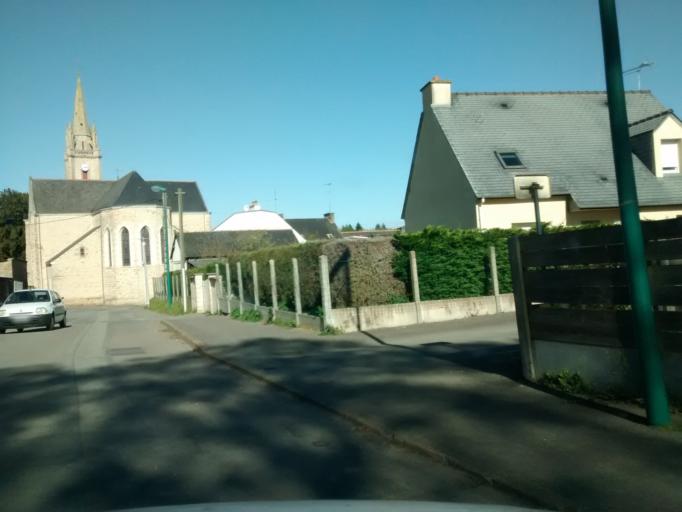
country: FR
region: Brittany
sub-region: Departement du Morbihan
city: Guillac
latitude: 47.8653
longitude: -2.4212
